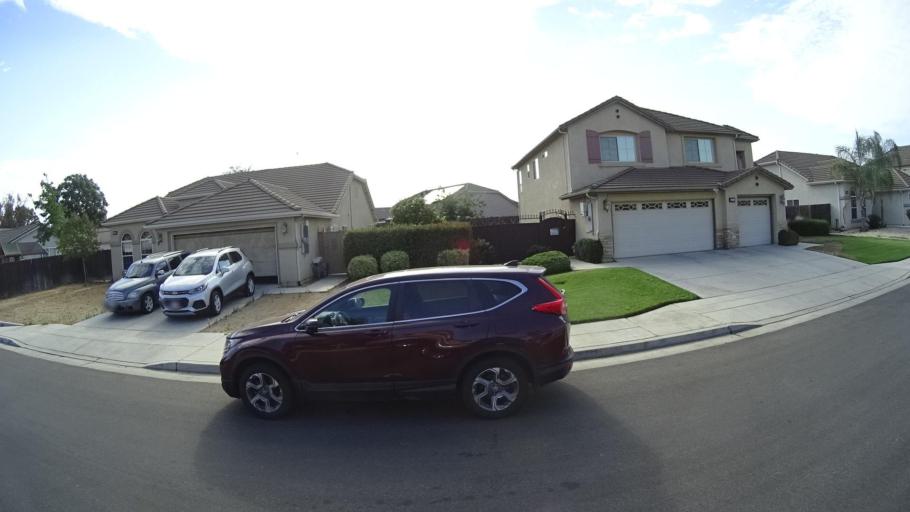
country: US
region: California
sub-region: Fresno County
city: Sunnyside
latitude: 36.7111
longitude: -119.6981
